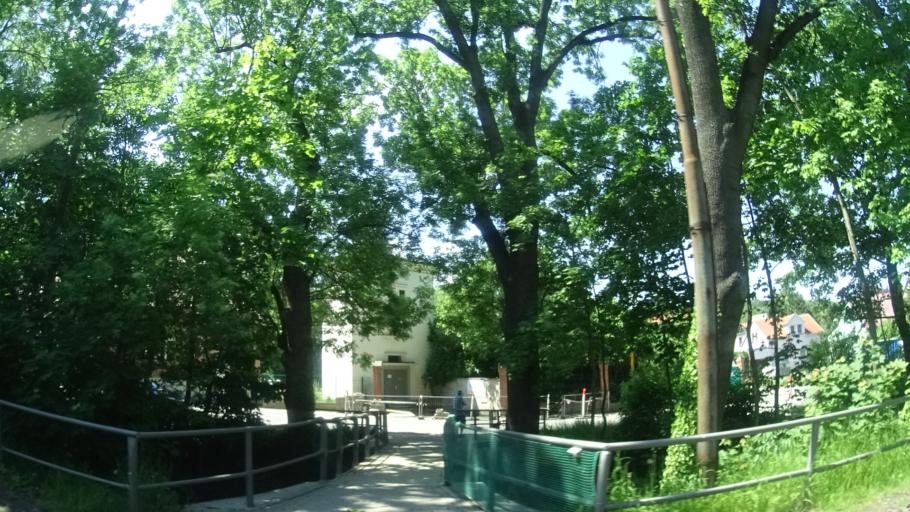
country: DE
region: Thuringia
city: Arnstadt
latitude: 50.8323
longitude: 10.9363
